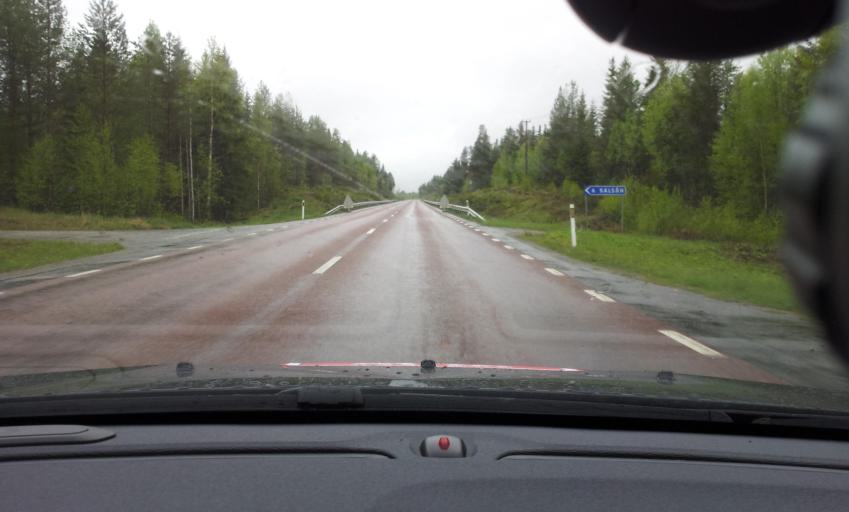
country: SE
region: Jaemtland
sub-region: Bergs Kommun
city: Hoverberg
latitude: 62.8708
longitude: 14.5222
